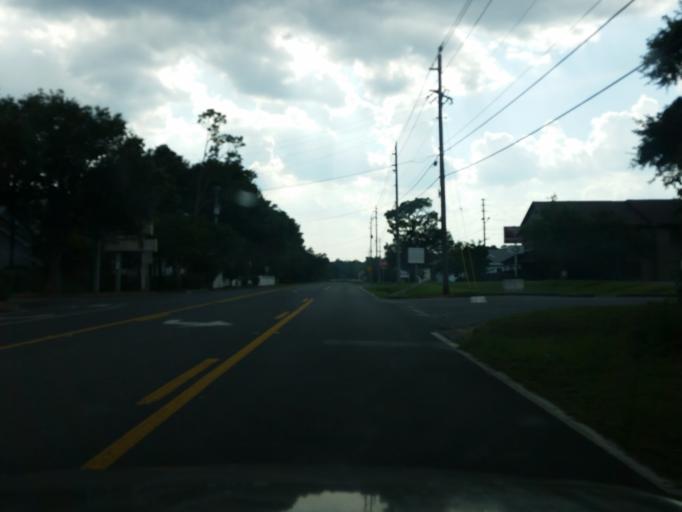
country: US
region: Florida
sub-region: Escambia County
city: Ferry Pass
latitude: 30.4942
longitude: -87.2268
